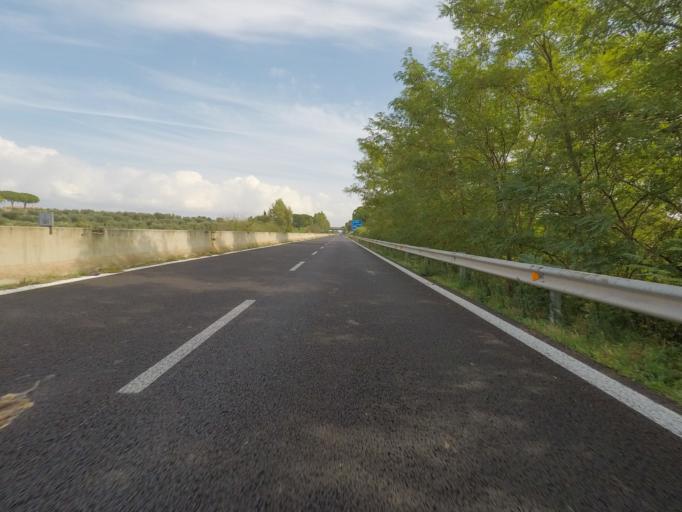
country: IT
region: Latium
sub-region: Provincia di Viterbo
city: Pescia Romana
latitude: 42.4039
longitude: 11.4940
